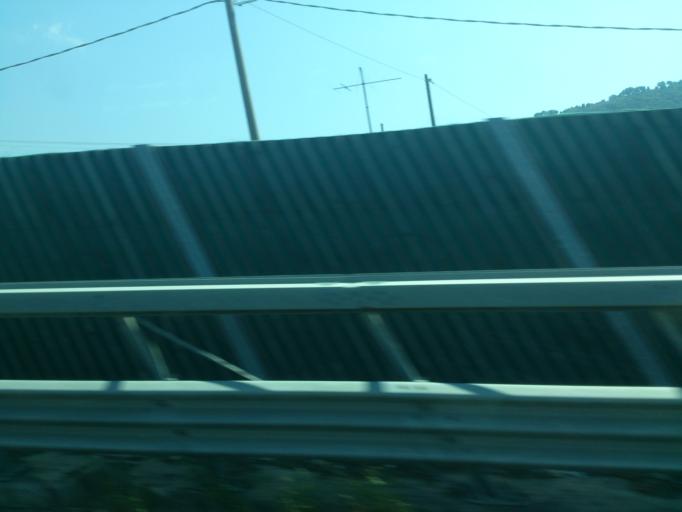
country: IT
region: Calabria
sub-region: Provincia di Catanzaro
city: Acconia
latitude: 38.8072
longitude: 16.2322
